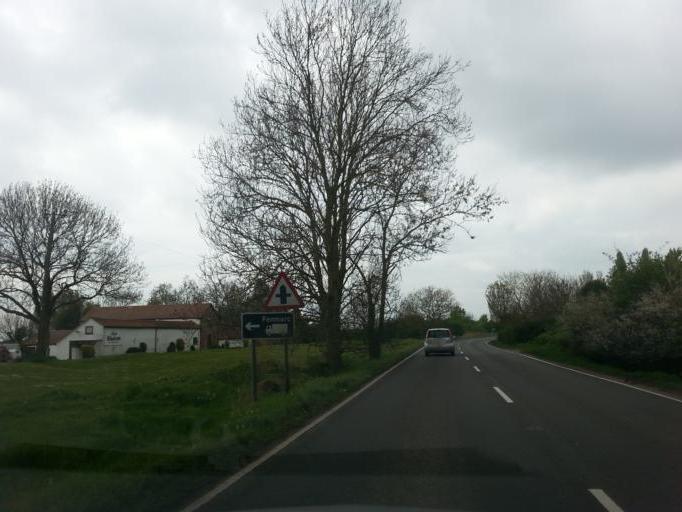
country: GB
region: England
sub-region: Norfolk
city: Emneth
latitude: 52.6337
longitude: 0.1935
